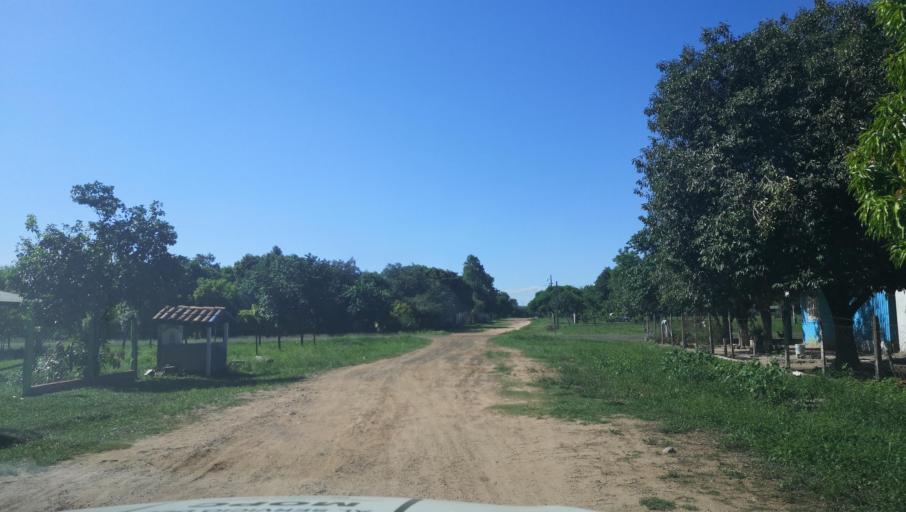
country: PY
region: Caaguazu
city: Carayao
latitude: -25.2059
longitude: -56.3973
